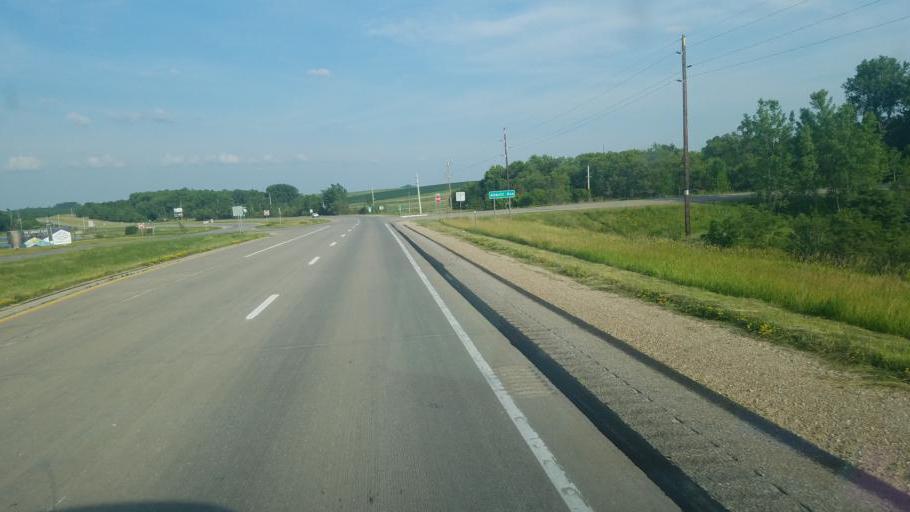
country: US
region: Iowa
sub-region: Marshall County
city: Marshalltown
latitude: 42.0079
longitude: -92.7686
